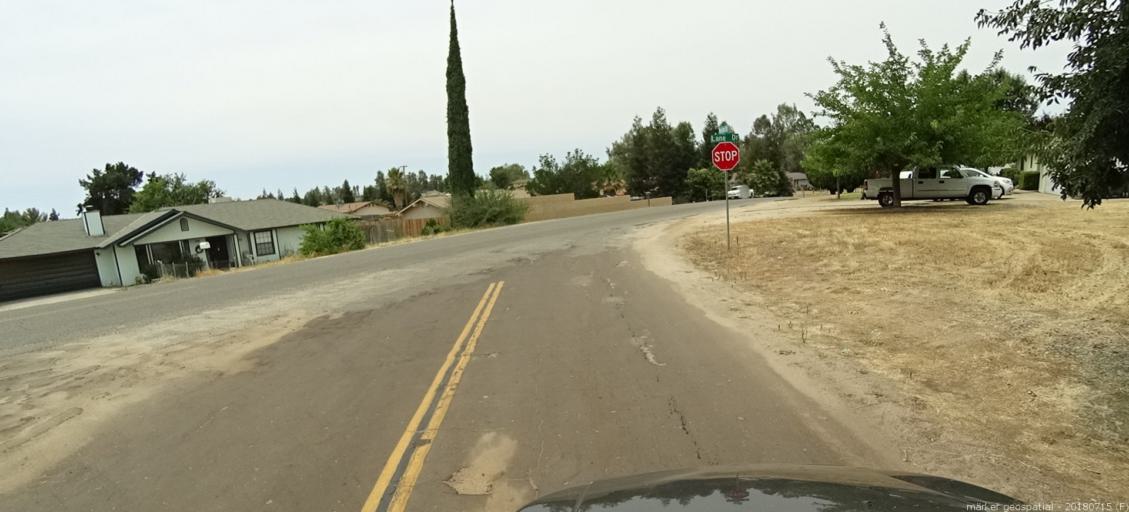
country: US
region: California
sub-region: Madera County
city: Madera Acres
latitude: 37.0050
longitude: -120.0833
